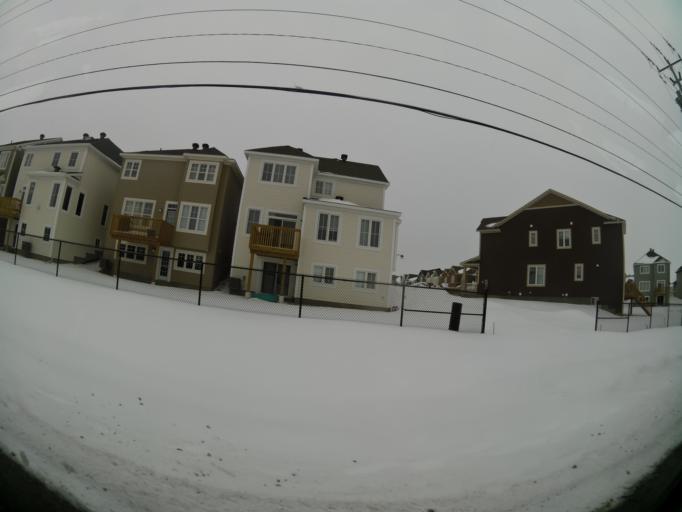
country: CA
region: Ontario
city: Bells Corners
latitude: 45.2824
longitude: -75.9282
